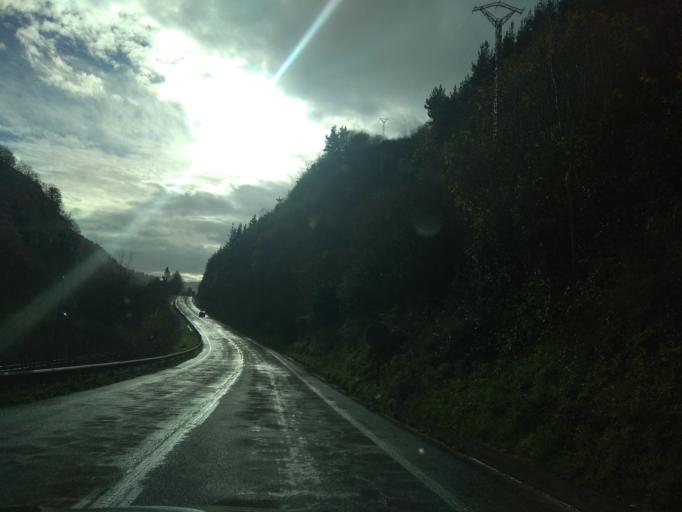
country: ES
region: Cantabria
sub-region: Provincia de Cantabria
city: San Pedro del Romeral
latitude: 43.1351
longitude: -3.9003
